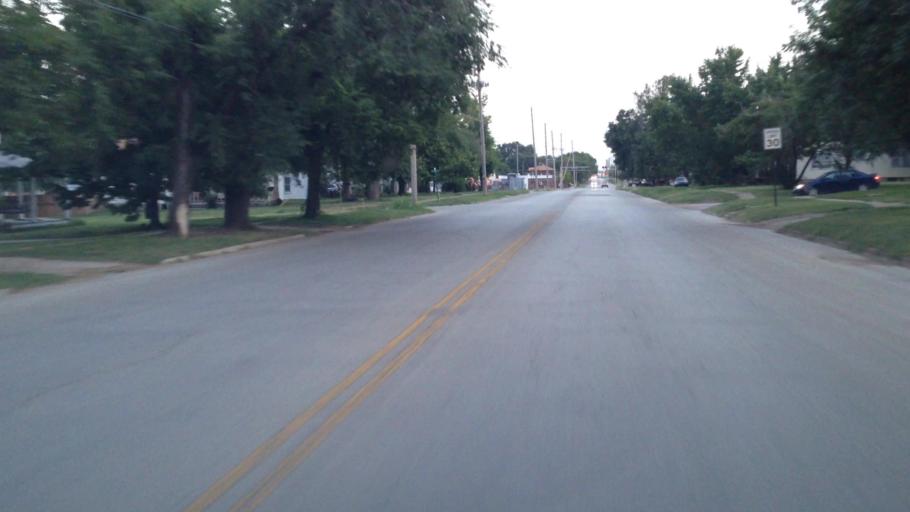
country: US
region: Kansas
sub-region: Montgomery County
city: Independence
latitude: 37.2350
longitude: -95.7107
